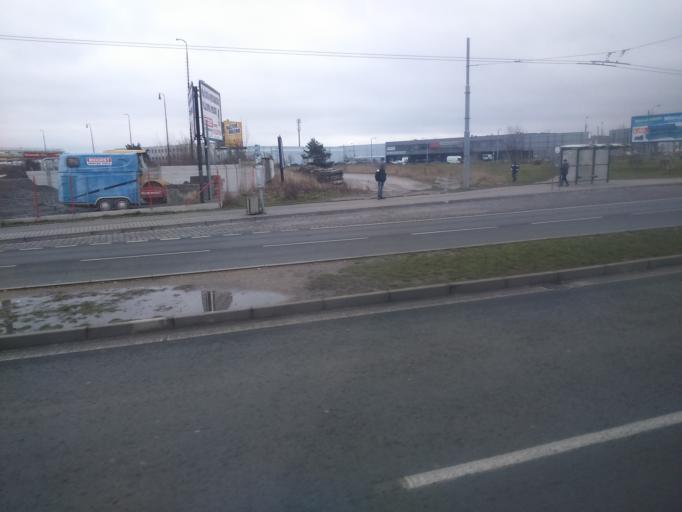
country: CZ
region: Plzensky
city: Vejprnice
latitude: 49.7329
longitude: 13.3218
